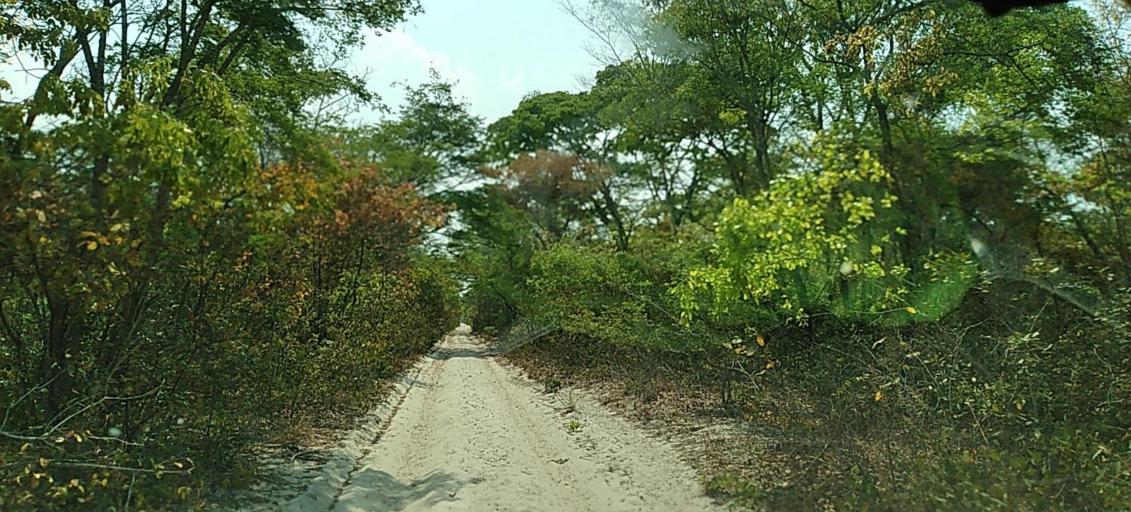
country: ZM
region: North-Western
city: Kabompo
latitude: -13.3900
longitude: 23.7814
